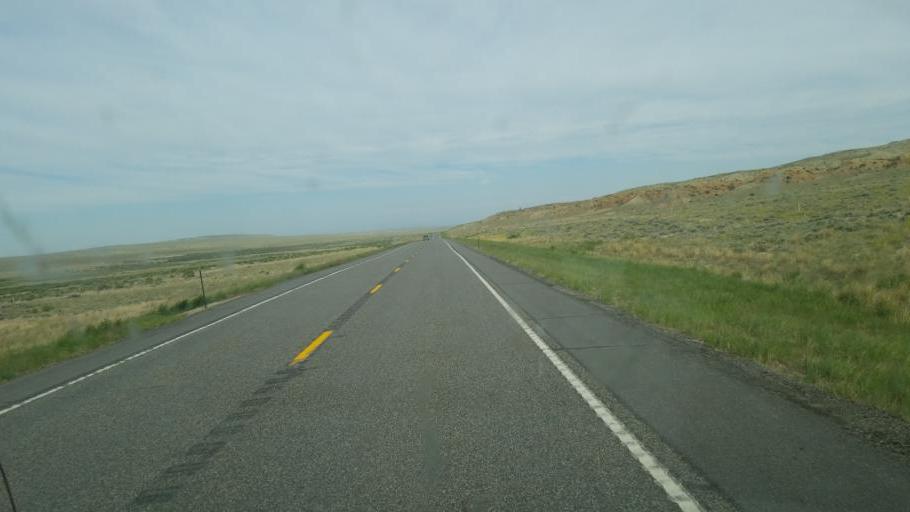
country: US
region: Wyoming
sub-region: Fremont County
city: Riverton
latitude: 43.2217
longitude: -107.9867
